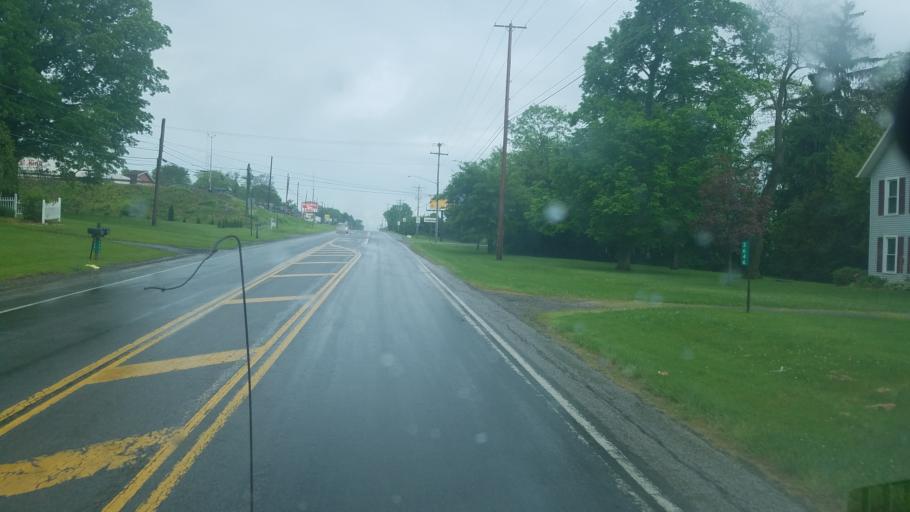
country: US
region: Ohio
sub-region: Wayne County
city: Wooster
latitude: 40.7959
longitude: -81.8949
